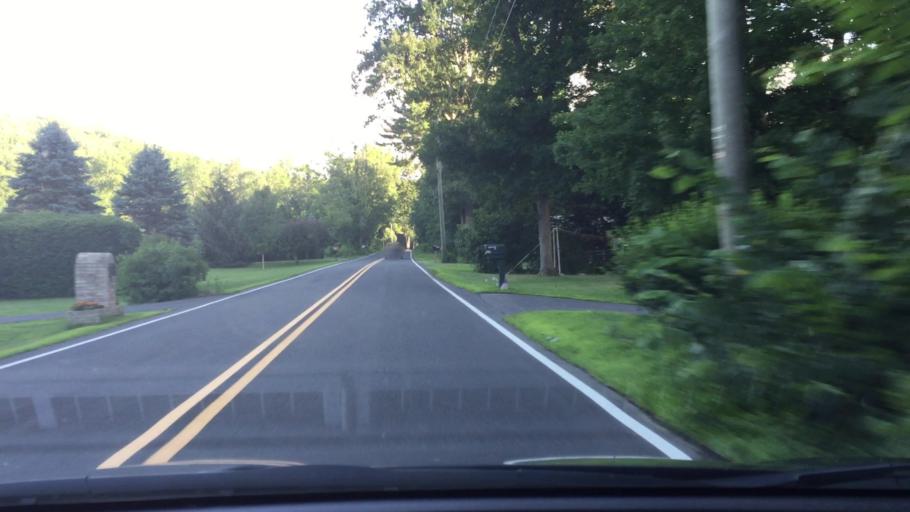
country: US
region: Massachusetts
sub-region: Hampshire County
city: Westhampton
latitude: 42.2245
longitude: -72.8555
